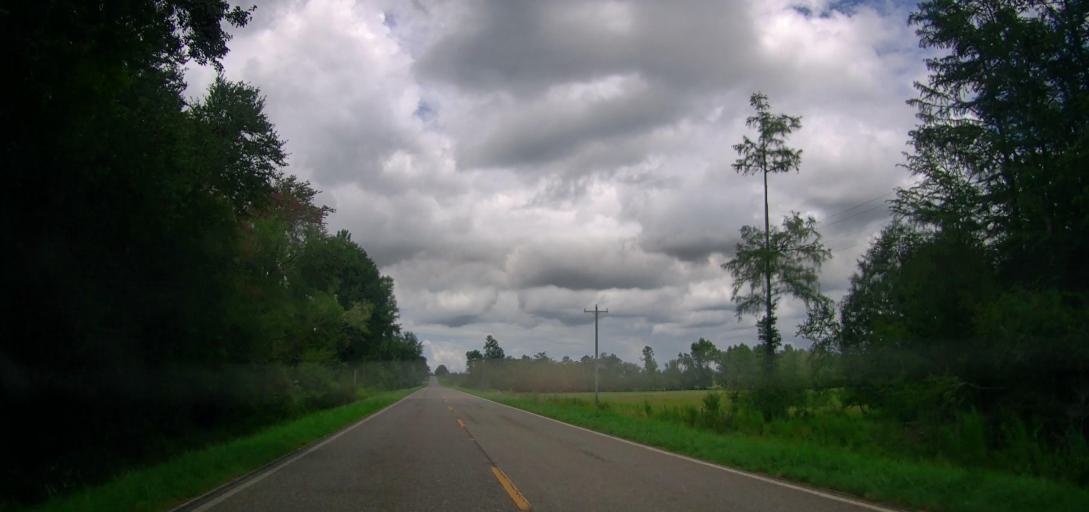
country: US
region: Georgia
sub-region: Wilcox County
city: Rochelle
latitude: 31.9097
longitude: -83.5532
